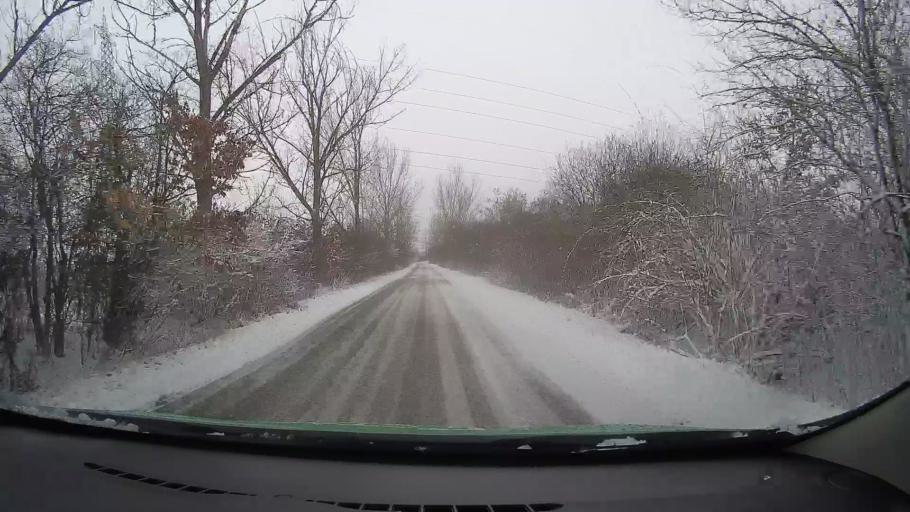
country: RO
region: Hunedoara
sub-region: Municipiul Hunedoara
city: Pestisu Mare
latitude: 45.8082
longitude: 22.9117
